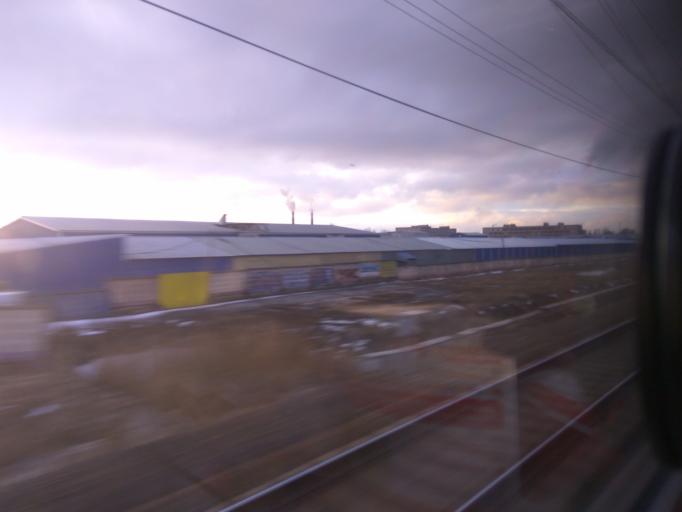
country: RU
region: St.-Petersburg
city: Kupchino
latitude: 59.8872
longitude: 30.3976
